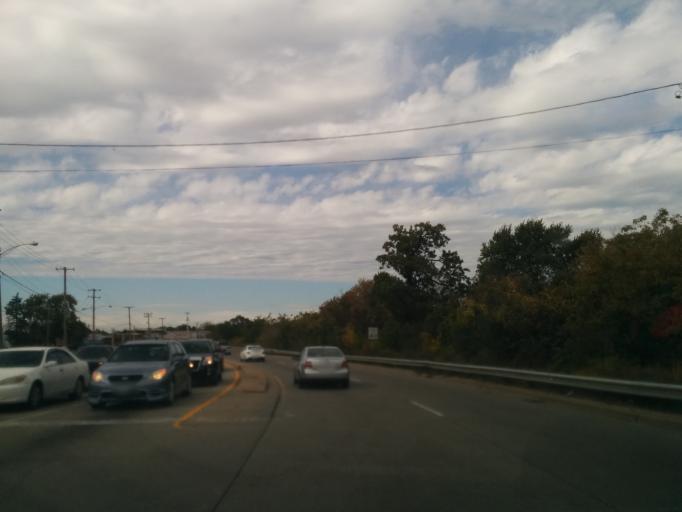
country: US
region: Illinois
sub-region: Cook County
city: Franklin Park
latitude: 41.9374
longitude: -87.8504
